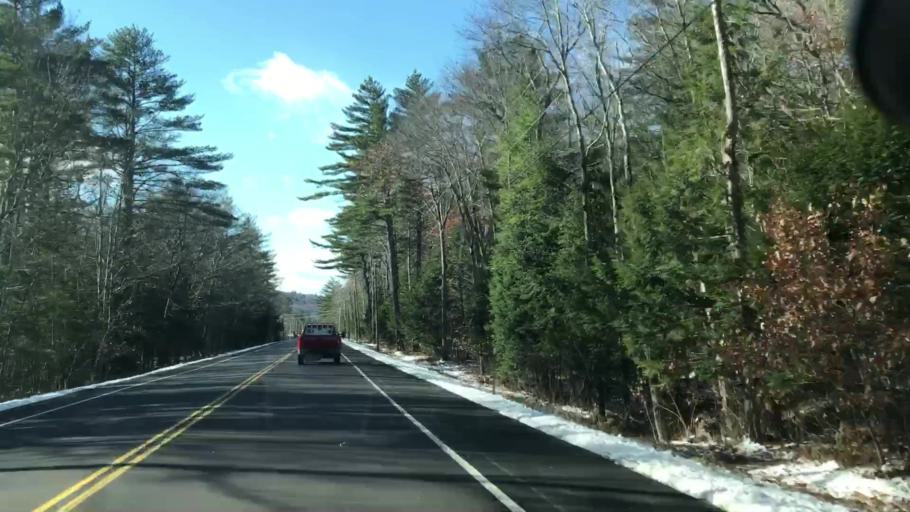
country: US
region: New Hampshire
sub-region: Carroll County
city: Freedom
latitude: 43.7975
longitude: -71.0097
